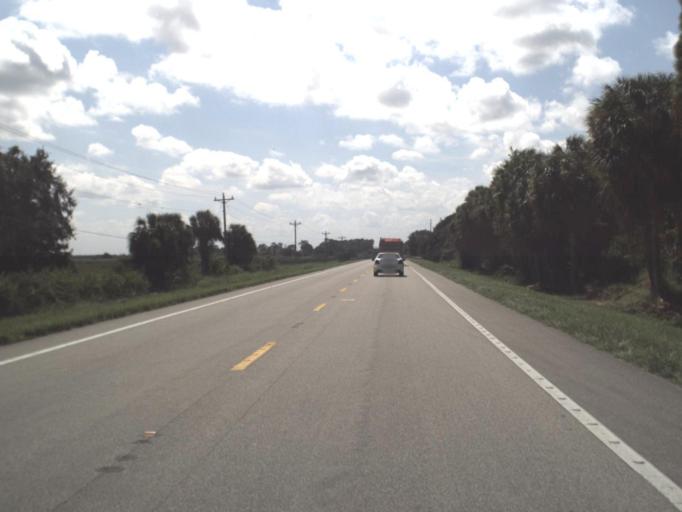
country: US
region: Florida
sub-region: Collier County
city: Immokalee
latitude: 26.5795
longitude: -81.4365
